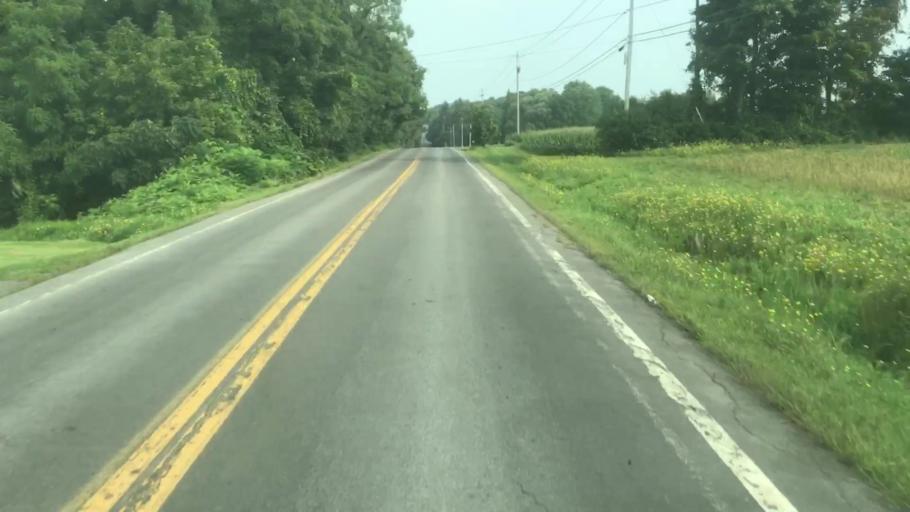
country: US
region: New York
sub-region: Onondaga County
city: Skaneateles
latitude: 42.8840
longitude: -76.4479
